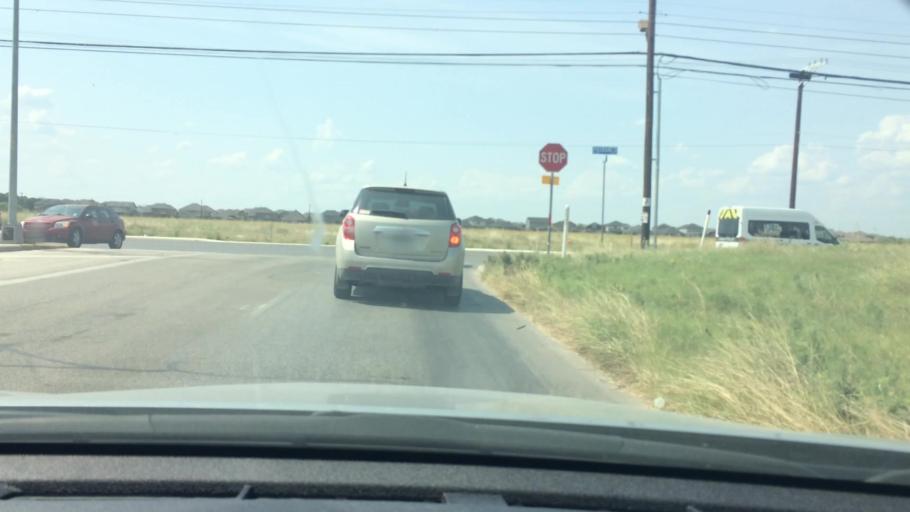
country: US
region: Texas
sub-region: Bexar County
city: Leon Valley
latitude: 29.4468
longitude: -98.6533
